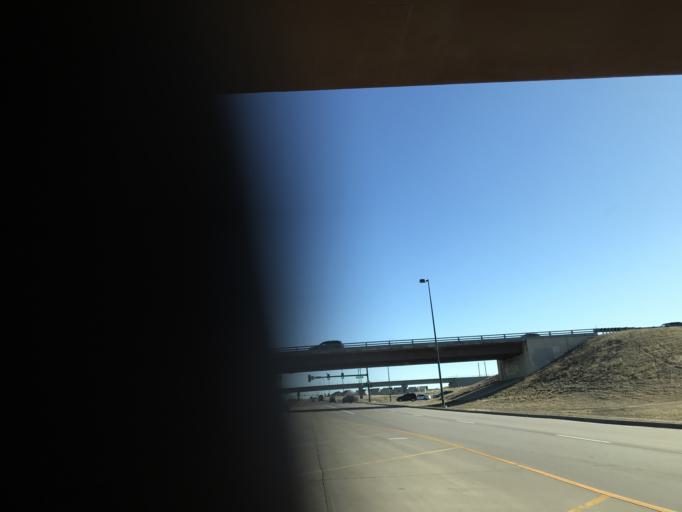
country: US
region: Colorado
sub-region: Adams County
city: Aurora
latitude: 39.7841
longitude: -104.7938
